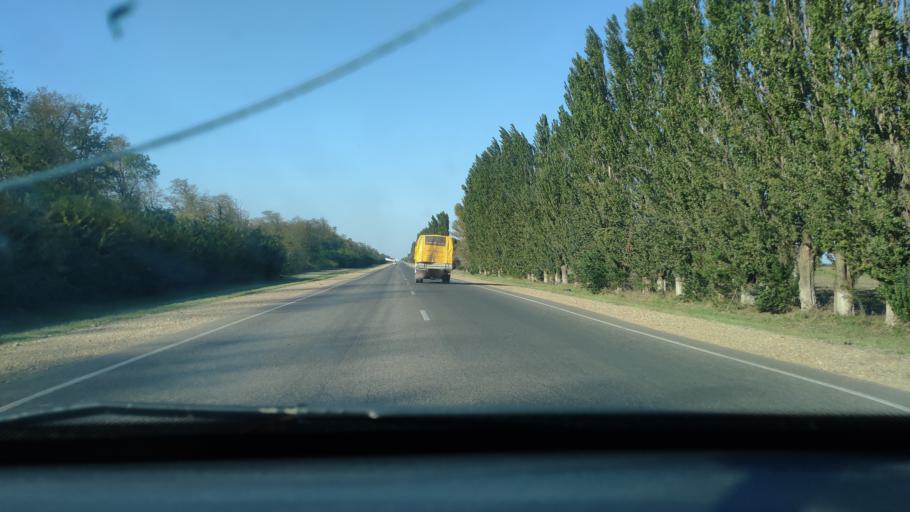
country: RU
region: Krasnodarskiy
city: Novotitarovskaya
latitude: 45.2654
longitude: 39.0016
